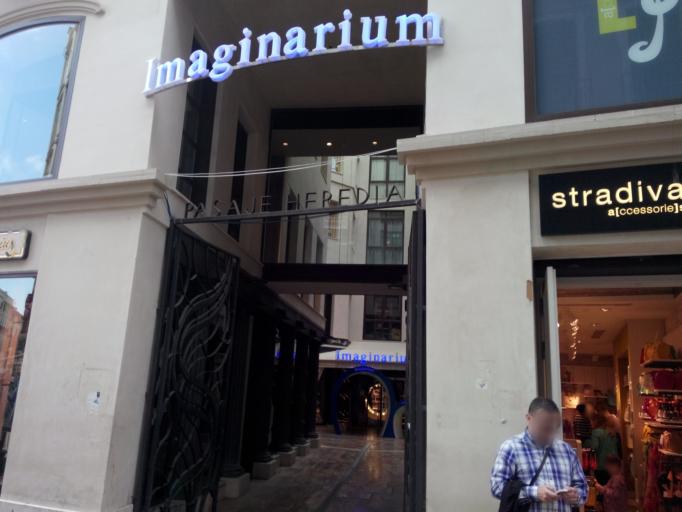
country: ES
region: Andalusia
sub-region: Provincia de Malaga
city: Malaga
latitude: 36.7217
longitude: -4.4214
